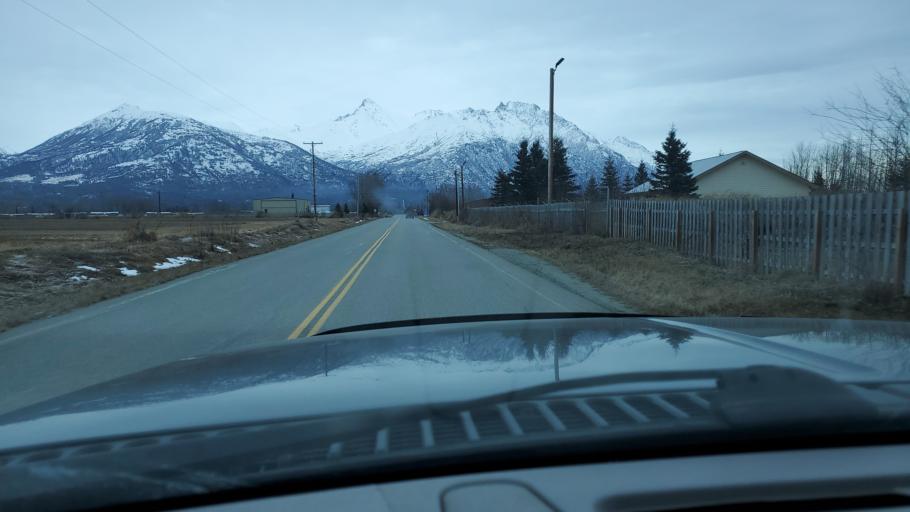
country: US
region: Alaska
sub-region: Matanuska-Susitna Borough
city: Palmer
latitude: 61.5994
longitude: -149.0997
